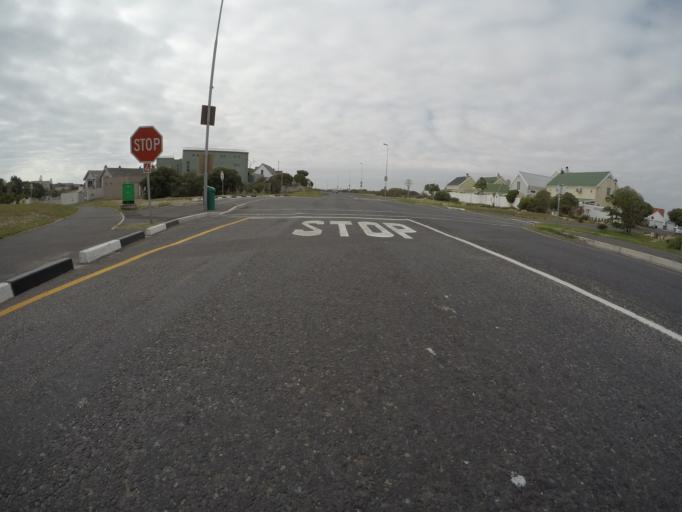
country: ZA
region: Western Cape
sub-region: City of Cape Town
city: Atlantis
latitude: -33.7112
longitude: 18.4464
